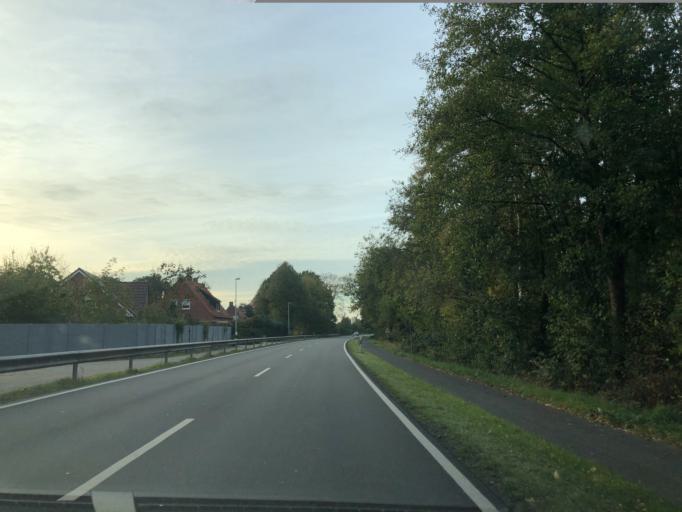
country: DE
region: Lower Saxony
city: Papenburg
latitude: 53.0643
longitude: 7.4026
